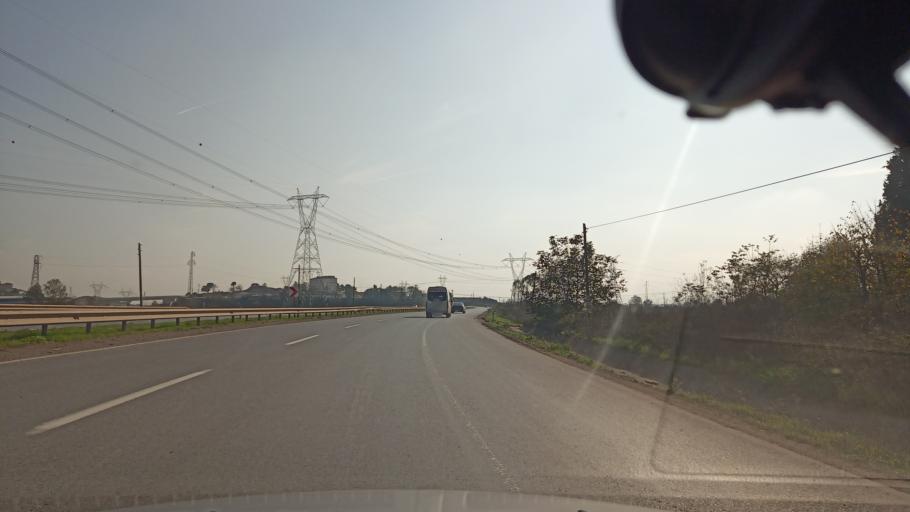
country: TR
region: Sakarya
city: Adapazari
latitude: 40.8280
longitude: 30.3898
